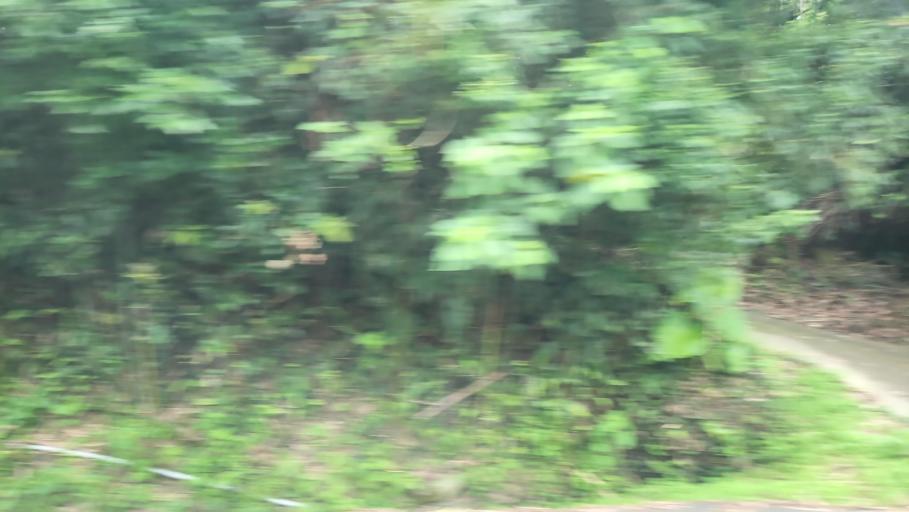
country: TW
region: Taiwan
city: Daxi
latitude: 24.8749
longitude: 121.4141
